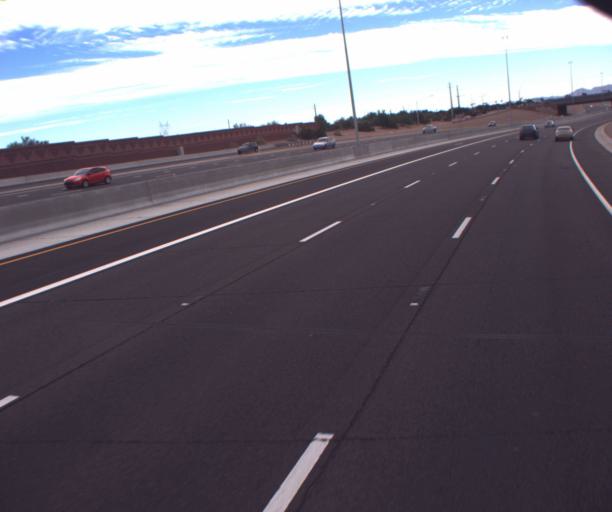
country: US
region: Arizona
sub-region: Pinal County
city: Apache Junction
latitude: 33.4263
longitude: -111.6361
